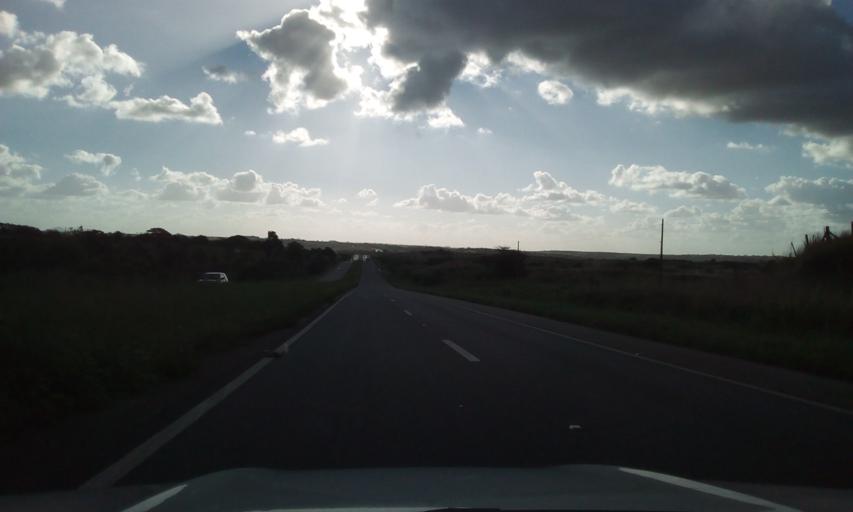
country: BR
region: Paraiba
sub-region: Cruz Do Espirito Santo
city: Cruz do Espirito Santo
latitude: -7.1980
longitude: -35.1668
